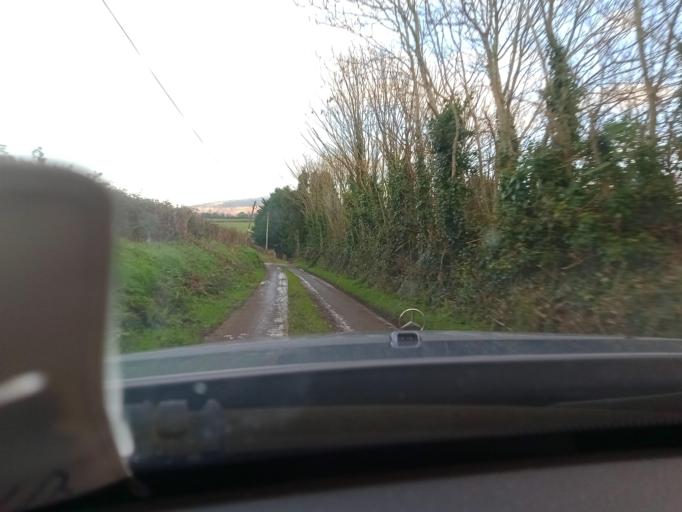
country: IE
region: Leinster
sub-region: Kilkenny
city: Graiguenamanagh
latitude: 52.5189
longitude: -6.9398
